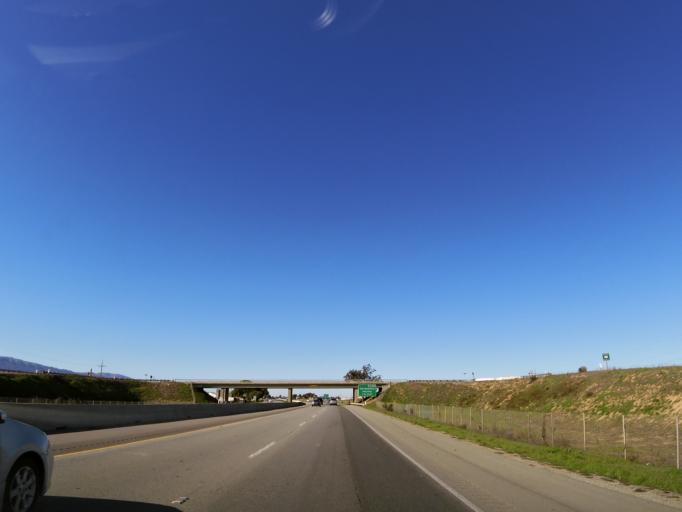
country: US
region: California
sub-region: Monterey County
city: Soledad
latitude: 36.4481
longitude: -121.3617
